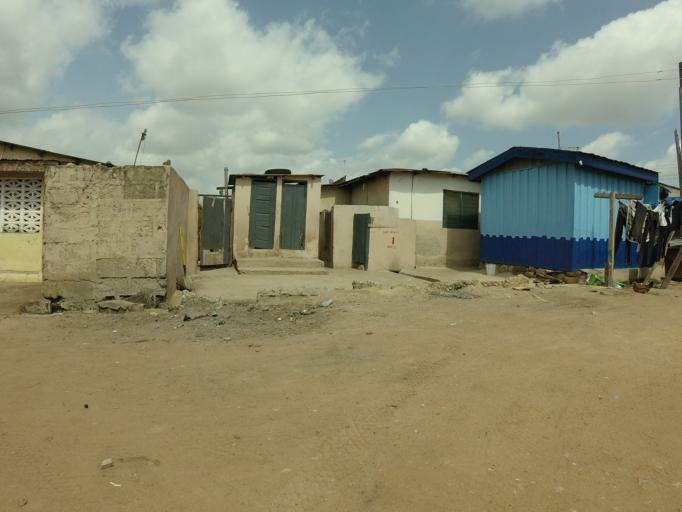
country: GH
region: Greater Accra
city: Dome
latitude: 5.6179
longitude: -0.2473
